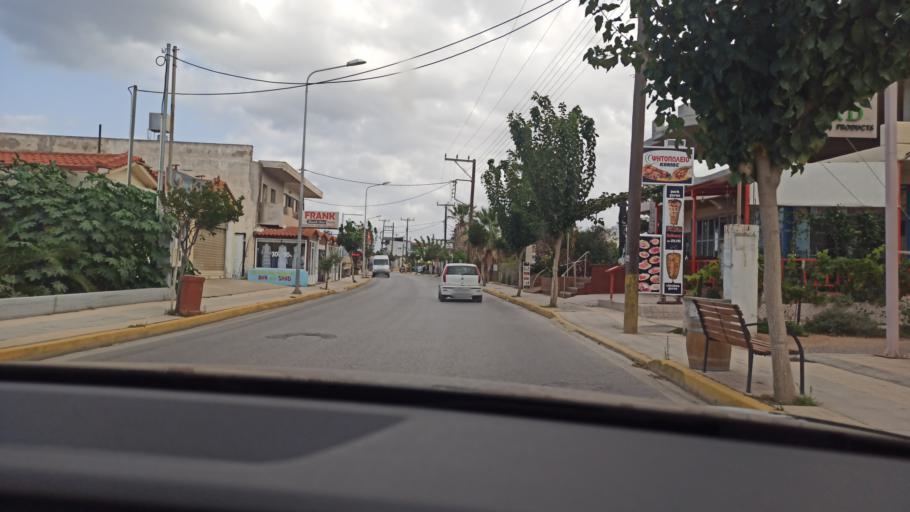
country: GR
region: Crete
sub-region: Nomos Irakleiou
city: Gazi
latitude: 35.3359
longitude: 25.0747
